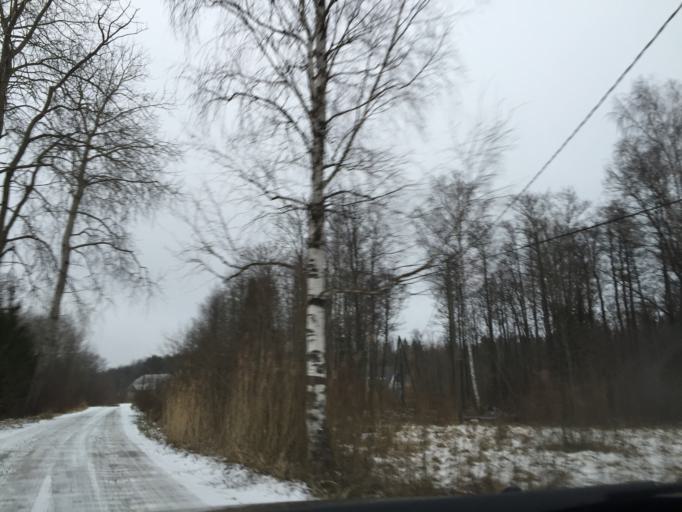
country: LV
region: Salacgrivas
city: Salacgriva
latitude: 57.5146
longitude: 24.3815
